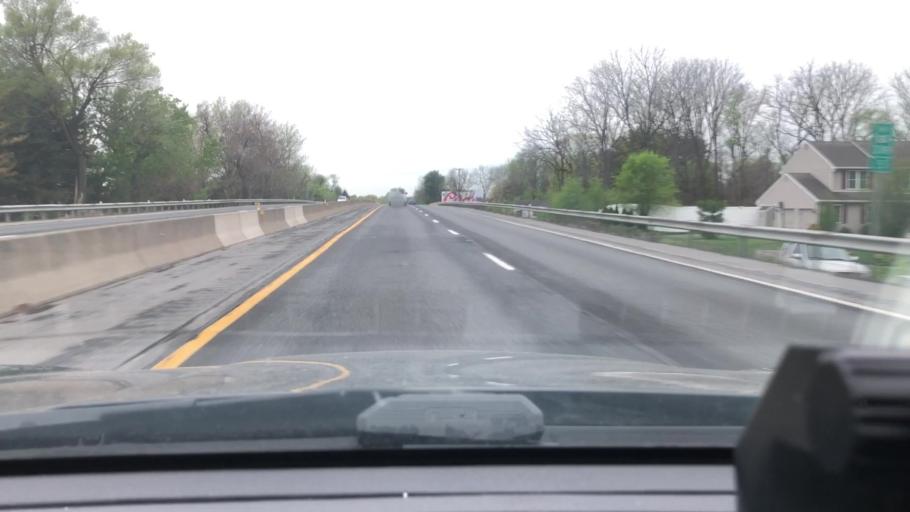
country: US
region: Pennsylvania
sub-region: Lehigh County
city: Allentown
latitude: 40.6125
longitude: -75.5159
